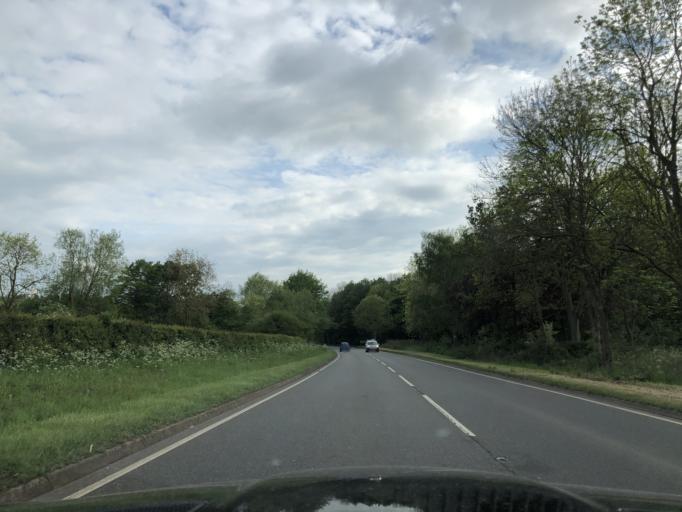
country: GB
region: England
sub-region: Warwickshire
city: Wellesbourne Mountford
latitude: 52.1309
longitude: -1.6150
